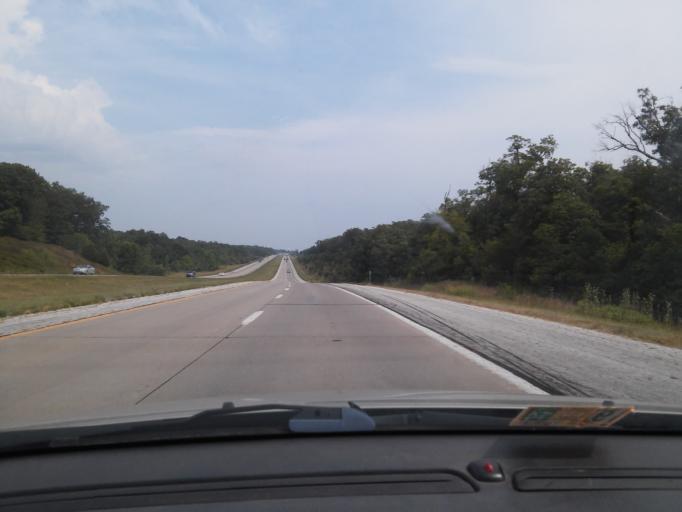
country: US
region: Missouri
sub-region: Callaway County
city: Fulton
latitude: 38.9783
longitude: -91.8943
